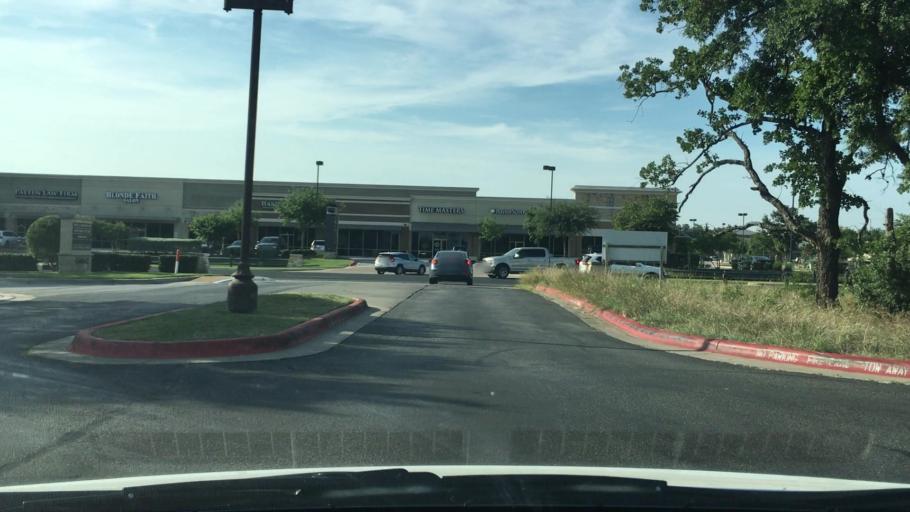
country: US
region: Texas
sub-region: Williamson County
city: Brushy Creek
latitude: 30.4991
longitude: -97.7743
